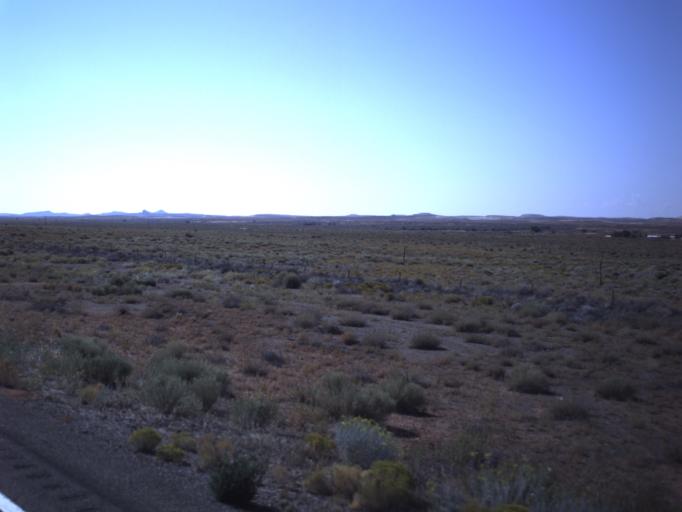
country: US
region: Utah
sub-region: San Juan County
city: Blanding
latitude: 37.1537
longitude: -109.5683
